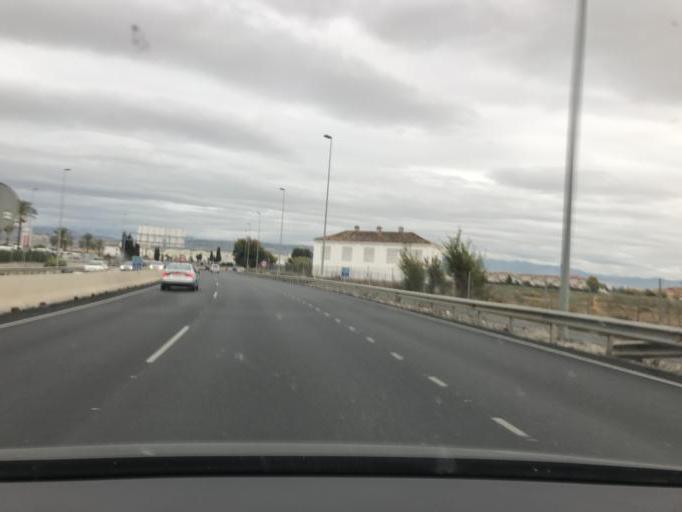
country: ES
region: Andalusia
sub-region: Provincia de Granada
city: Peligros
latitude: 37.2197
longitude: -3.6283
